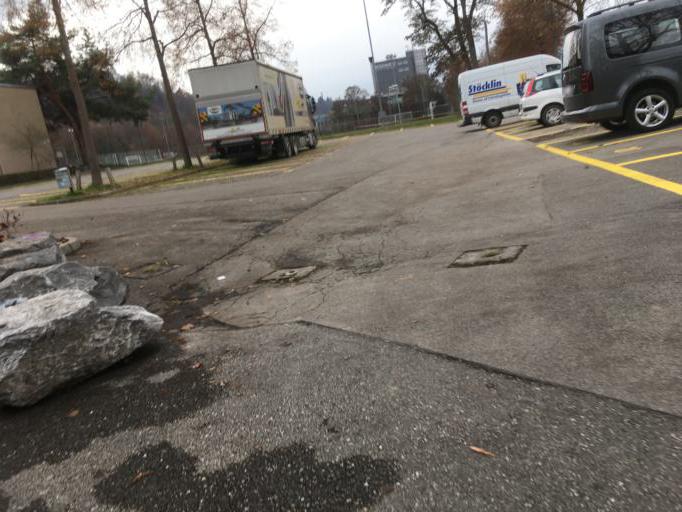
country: CH
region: Bern
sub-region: Bern-Mittelland District
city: Koniz
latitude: 46.9412
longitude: 7.4019
